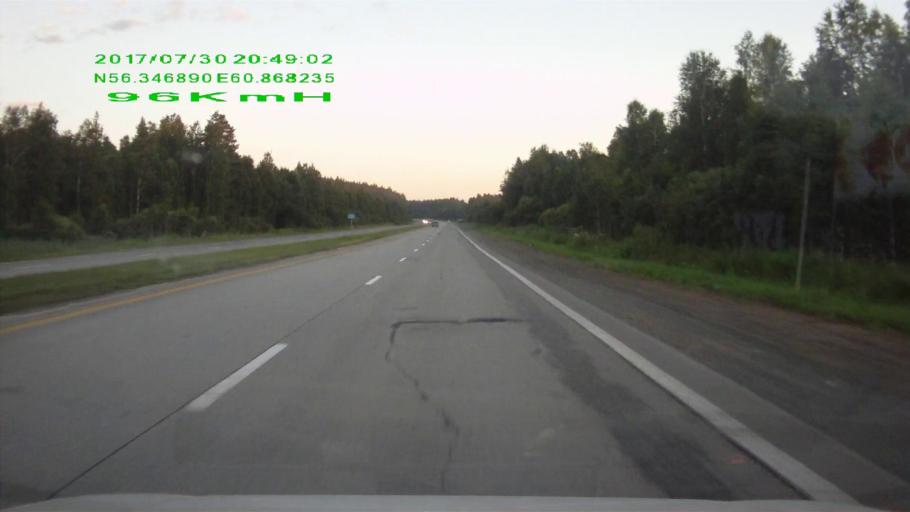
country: RU
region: Sverdlovsk
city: Shchelkun
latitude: 56.3463
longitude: 60.8681
